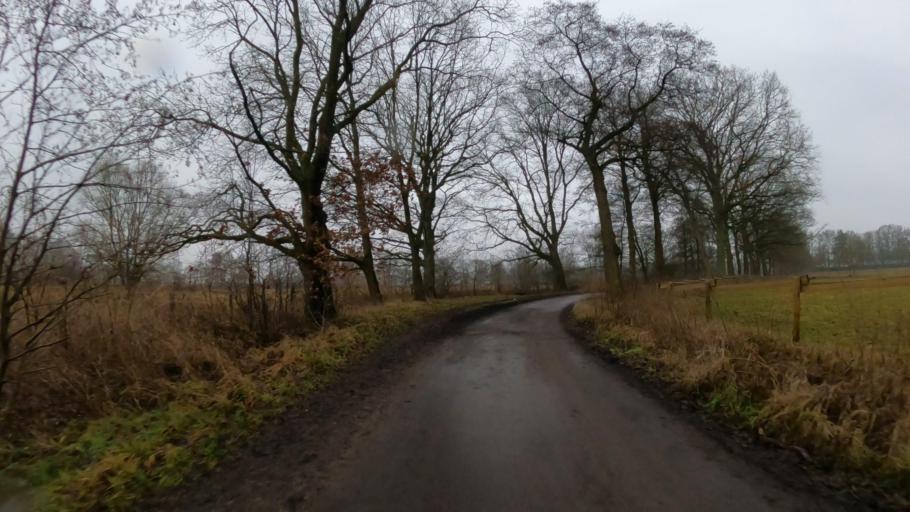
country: DE
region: Schleswig-Holstein
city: Appen
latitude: 53.5975
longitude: 9.7747
